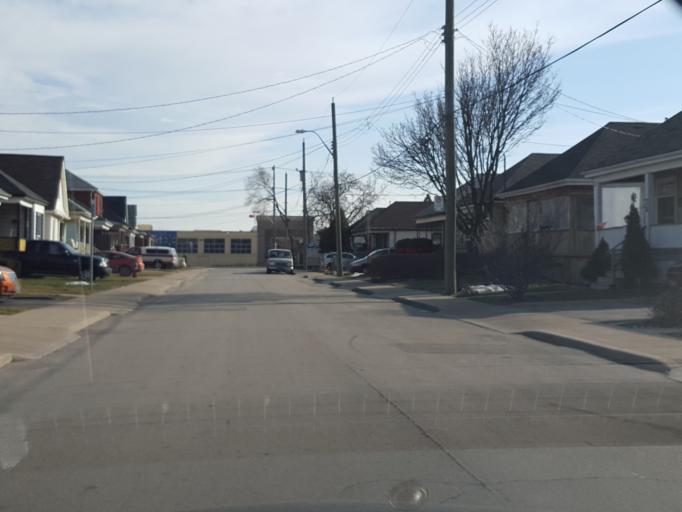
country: CA
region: Ontario
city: Hamilton
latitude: 43.2528
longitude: -79.8173
